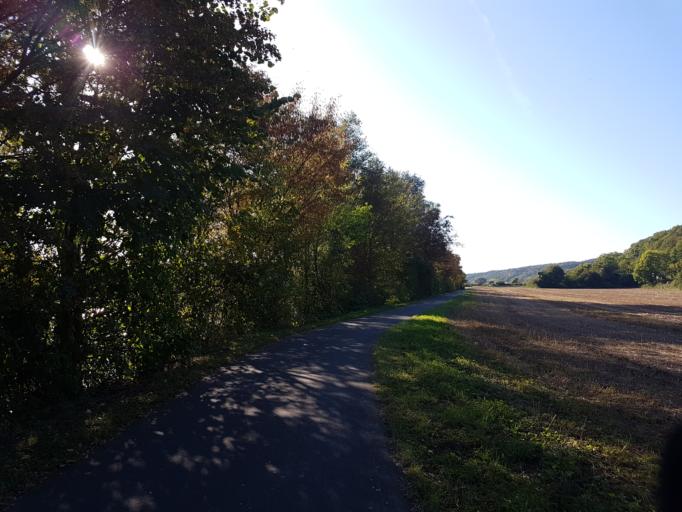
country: DE
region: North Rhine-Westphalia
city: Porta Westfalica
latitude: 52.2404
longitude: 8.8901
